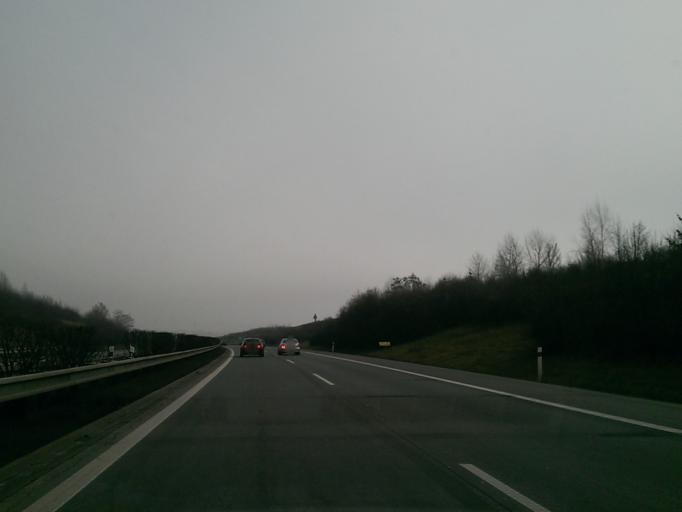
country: CZ
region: Olomoucky
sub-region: Okres Olomouc
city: Olomouc
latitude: 49.5486
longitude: 17.2398
